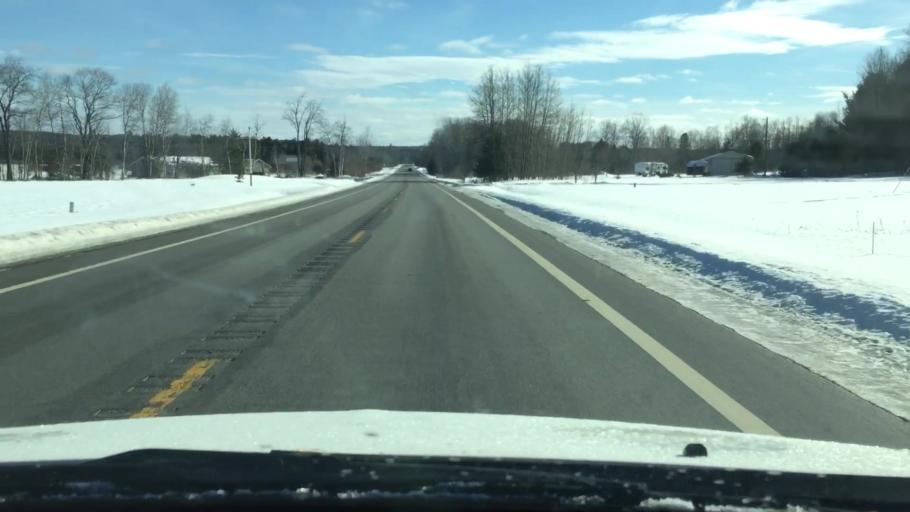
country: US
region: Michigan
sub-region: Charlevoix County
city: East Jordan
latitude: 45.0652
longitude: -85.0823
